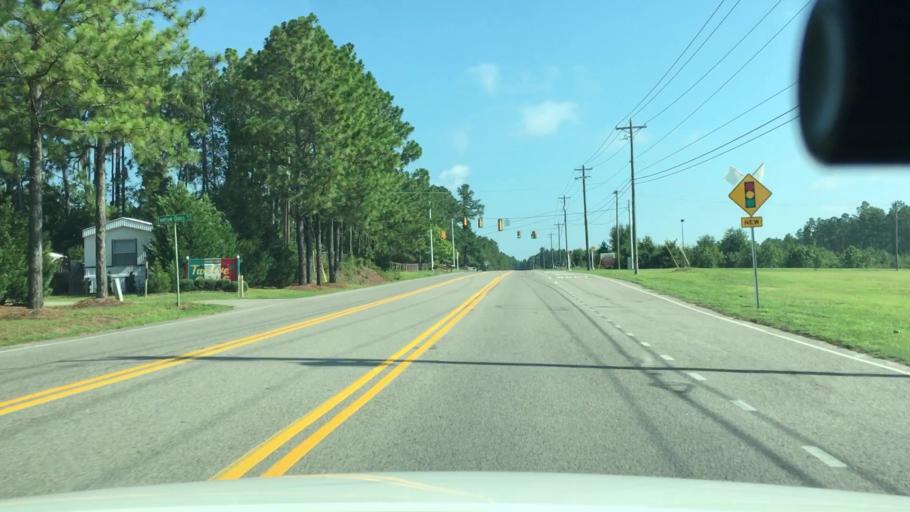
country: US
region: South Carolina
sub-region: Aiken County
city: Graniteville
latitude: 33.5828
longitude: -81.8361
